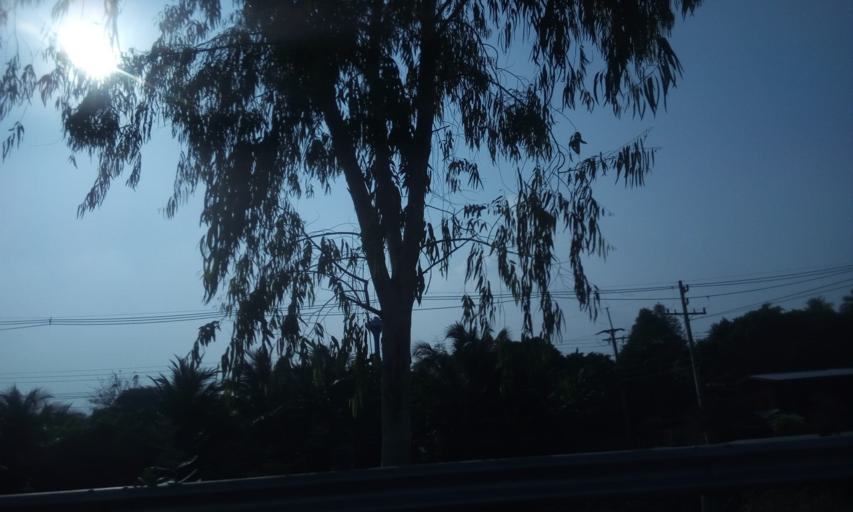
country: TH
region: Sing Buri
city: Sing Buri
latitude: 14.8641
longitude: 100.4049
